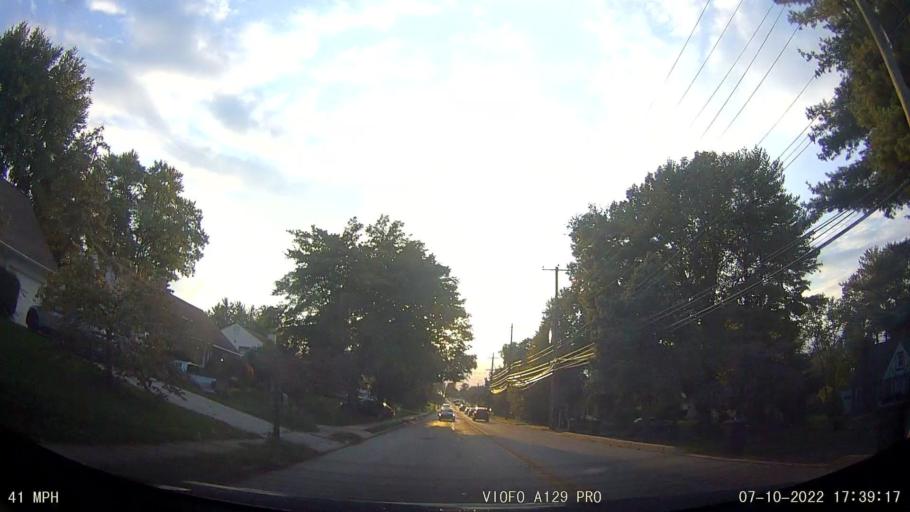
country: US
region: Pennsylvania
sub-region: Montgomery County
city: King of Prussia
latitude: 40.1031
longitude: -75.3867
